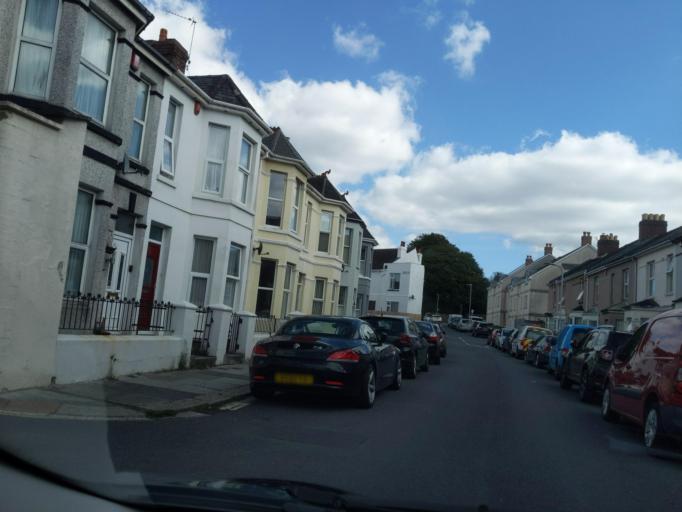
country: GB
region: England
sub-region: Plymouth
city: Plymouth
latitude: 50.3878
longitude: -4.1378
